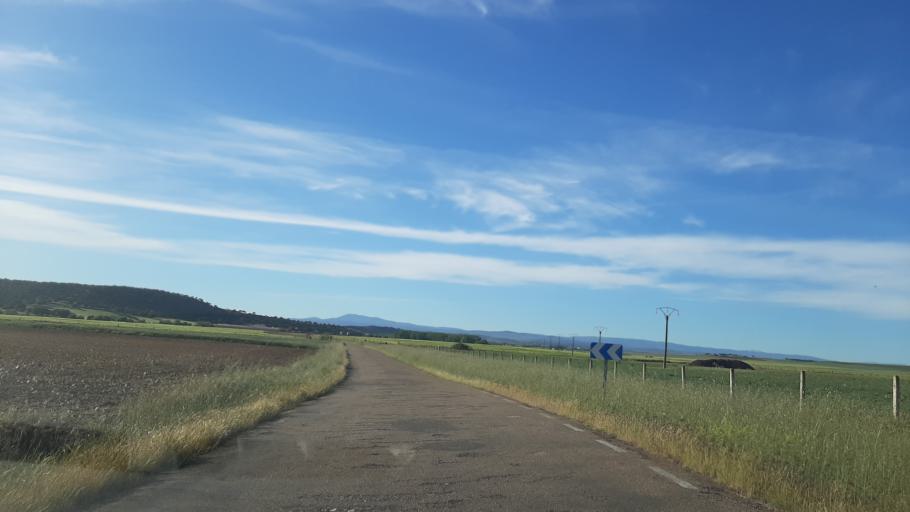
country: ES
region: Castille and Leon
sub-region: Provincia de Salamanca
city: Pedrosillo de Alba
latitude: 40.8036
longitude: -5.3794
